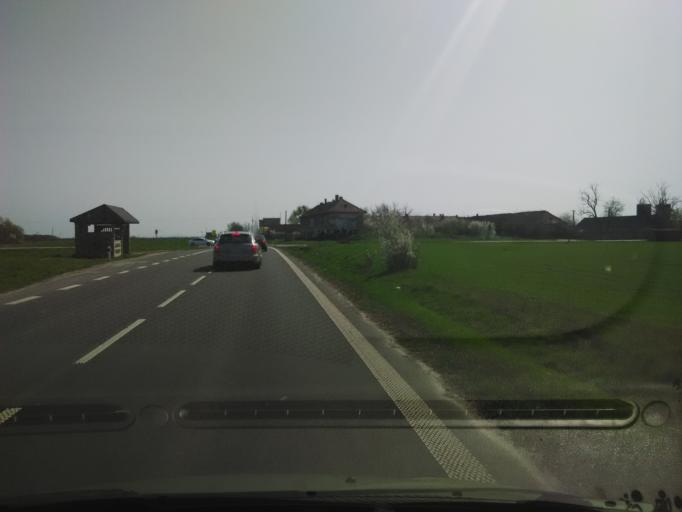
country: SK
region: Nitriansky
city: Surany
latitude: 48.0633
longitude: 18.0986
